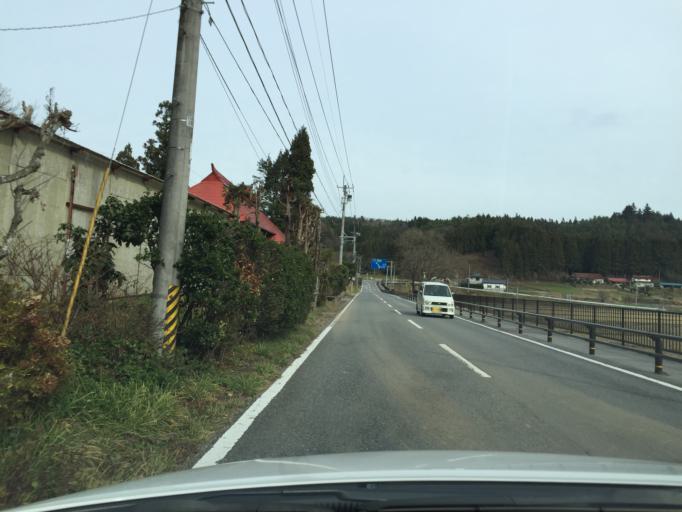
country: JP
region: Fukushima
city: Ishikawa
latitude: 37.1945
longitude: 140.6262
